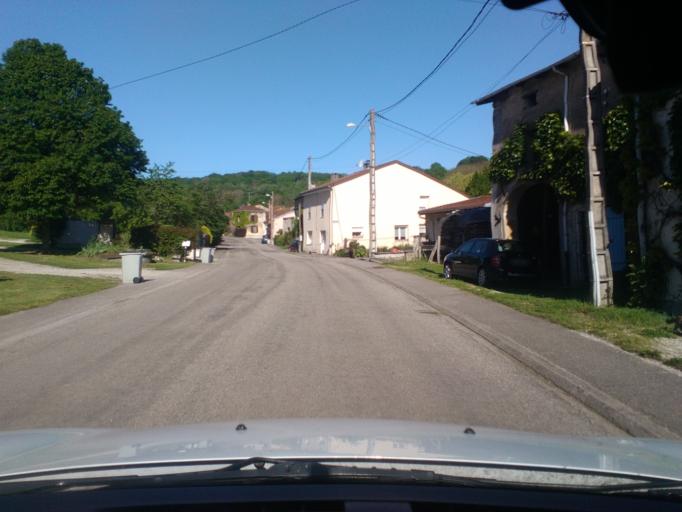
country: FR
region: Lorraine
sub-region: Departement des Vosges
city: Charmes
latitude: 48.3345
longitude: 6.2337
